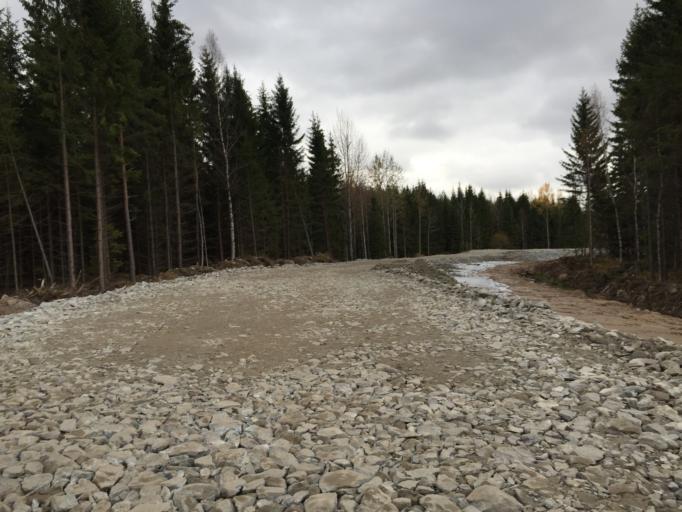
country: SE
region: Vaestmanland
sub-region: Hallstahammars Kommun
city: Hallstahammar
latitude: 59.6392
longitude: 16.2067
